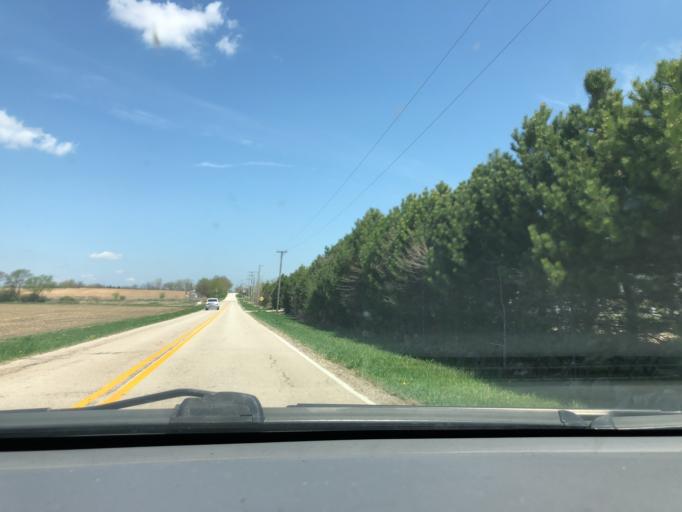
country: US
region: Illinois
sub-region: Kane County
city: Hampshire
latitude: 42.0917
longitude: -88.4814
